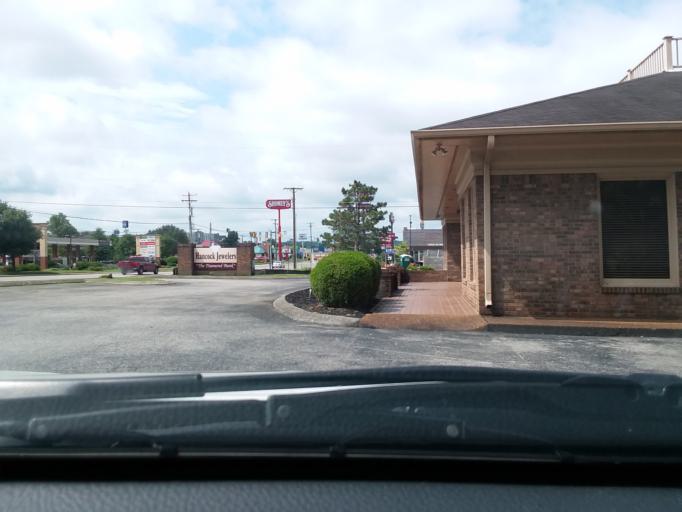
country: US
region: Tennessee
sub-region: Davidson County
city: Goodlettsville
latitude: 36.3275
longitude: -86.6998
